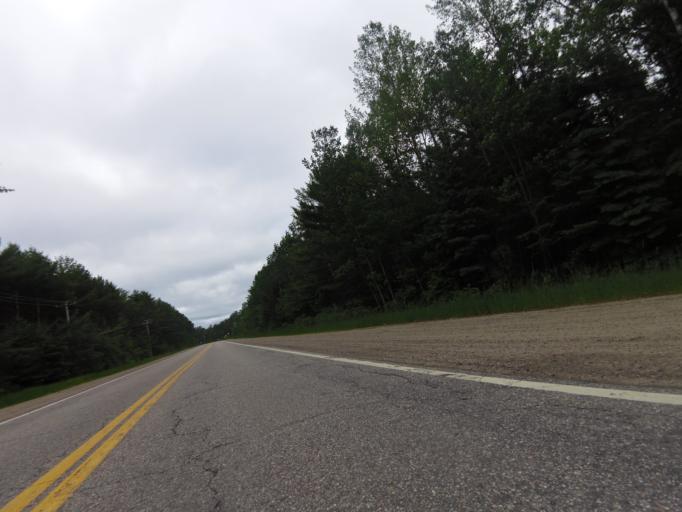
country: CA
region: Quebec
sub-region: Outaouais
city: Shawville
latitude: 45.8582
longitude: -76.4175
